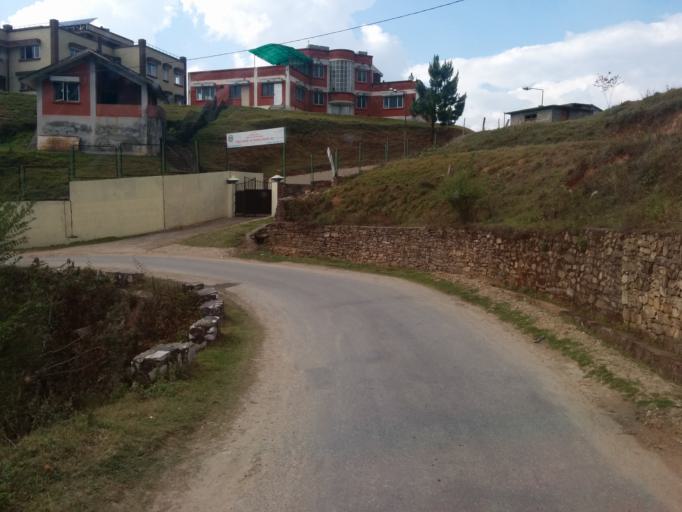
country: NP
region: Central Region
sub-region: Bagmati Zone
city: Nagarkot
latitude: 27.7113
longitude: 85.4930
